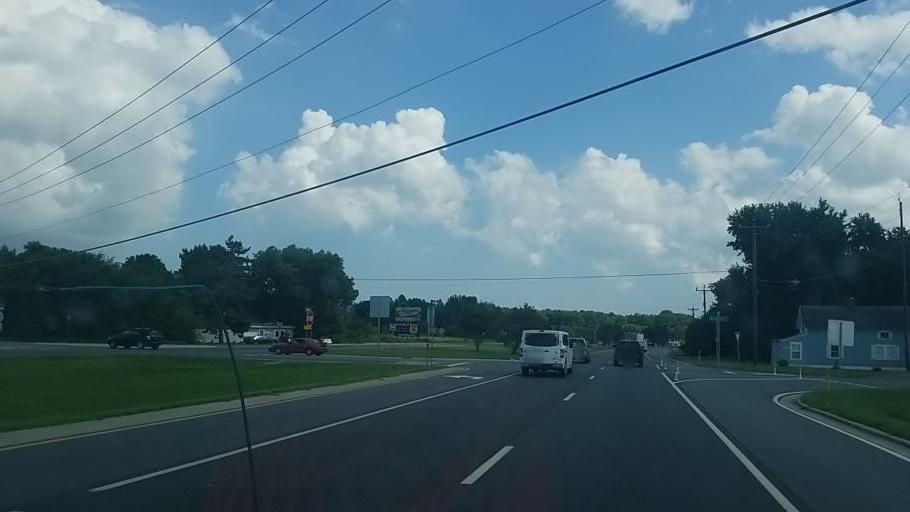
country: US
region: Delaware
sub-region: Sussex County
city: Selbyville
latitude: 38.5178
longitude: -75.2406
